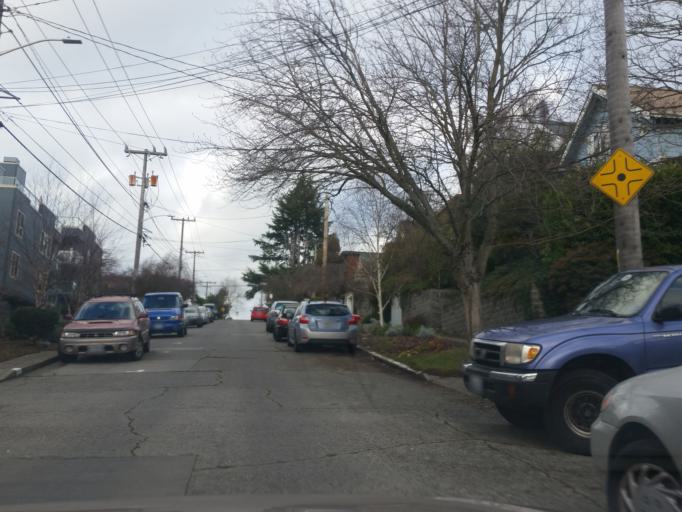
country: US
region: Washington
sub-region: King County
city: Seattle
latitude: 47.6605
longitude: -122.3555
